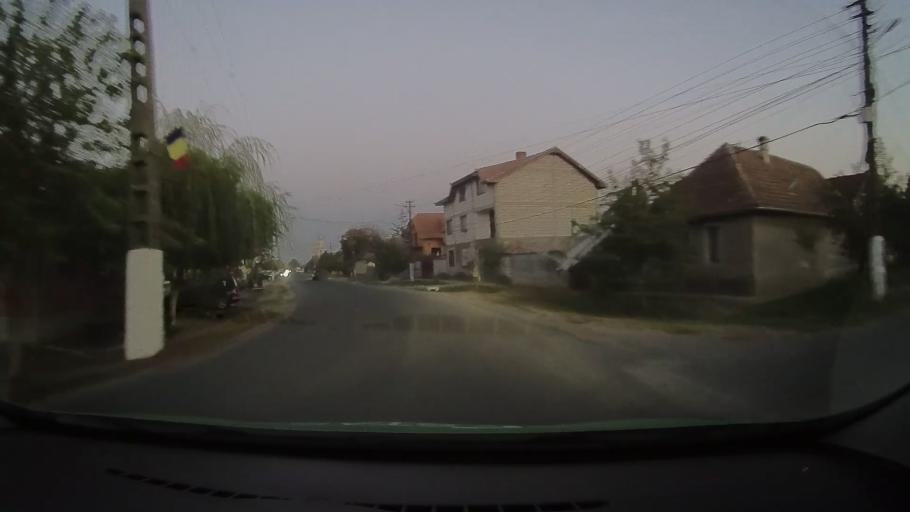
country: RO
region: Arad
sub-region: Comuna Livada
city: Livada
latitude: 46.2259
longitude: 21.3824
